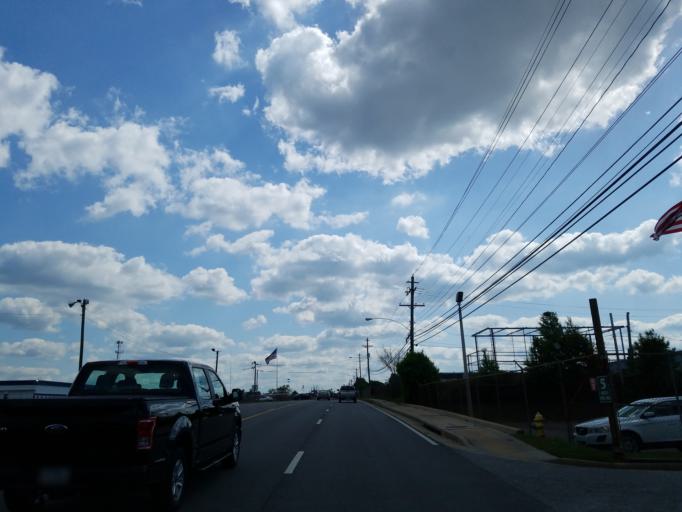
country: US
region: Georgia
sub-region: Peach County
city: Fort Valley
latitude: 32.5622
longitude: -83.8803
